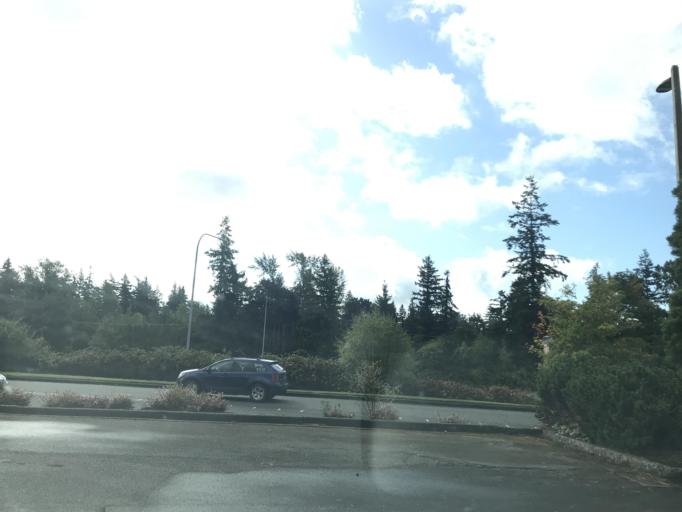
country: US
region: Washington
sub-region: Whatcom County
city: Bellingham
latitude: 48.7839
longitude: -122.4937
